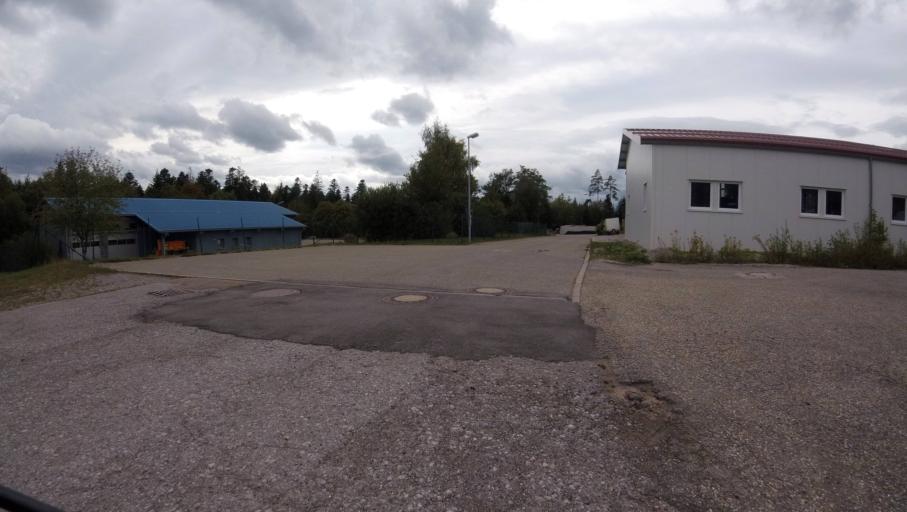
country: DE
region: Baden-Wuerttemberg
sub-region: Karlsruhe Region
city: Enzklosterle
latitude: 48.6017
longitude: 8.4324
